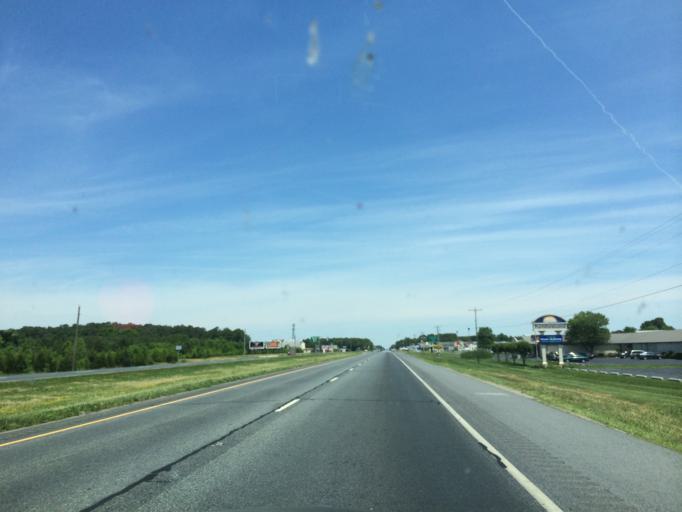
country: US
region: Delaware
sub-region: Sussex County
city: Delmar
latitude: 38.4596
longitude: -75.5580
